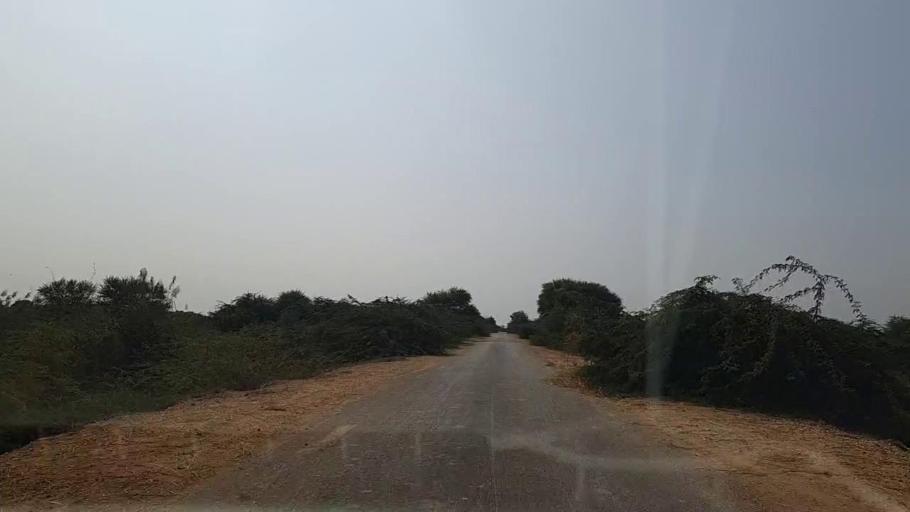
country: PK
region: Sindh
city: Chuhar Jamali
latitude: 24.2696
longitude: 67.9119
